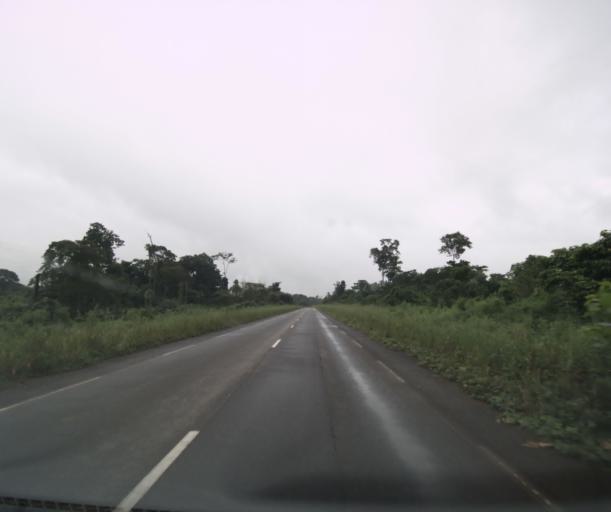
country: CM
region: Littoral
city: Edea
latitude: 3.4787
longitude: 10.1317
